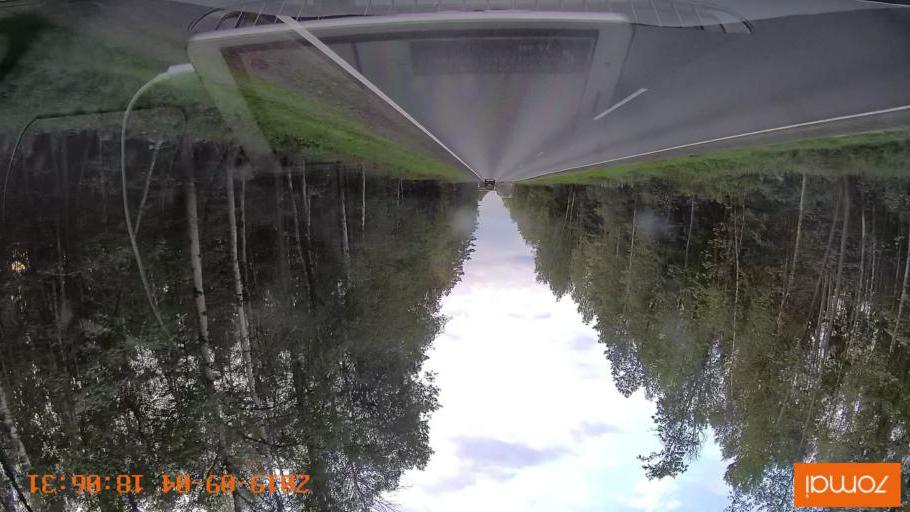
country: RU
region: Moskovskaya
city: Khorlovo
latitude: 55.4304
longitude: 38.8142
